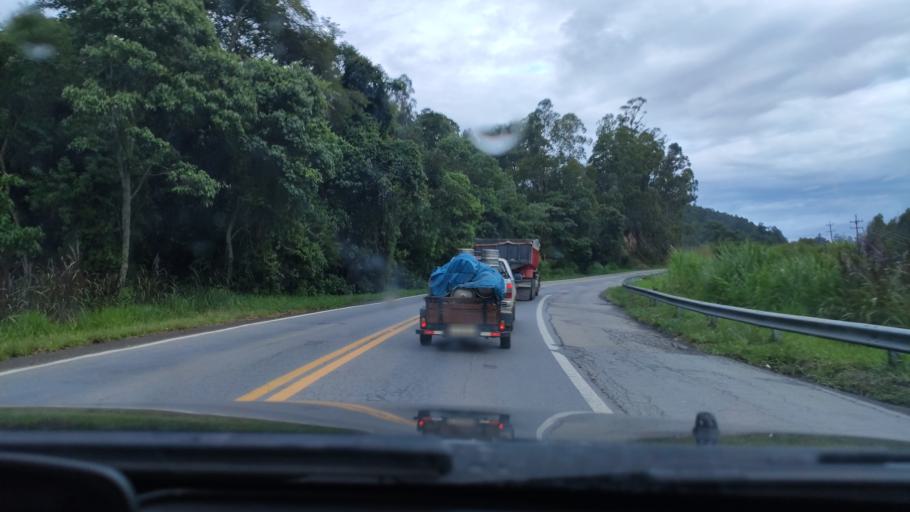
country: BR
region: Sao Paulo
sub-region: Braganca Paulista
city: Braganca Paulista
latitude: -22.8276
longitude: -46.5580
